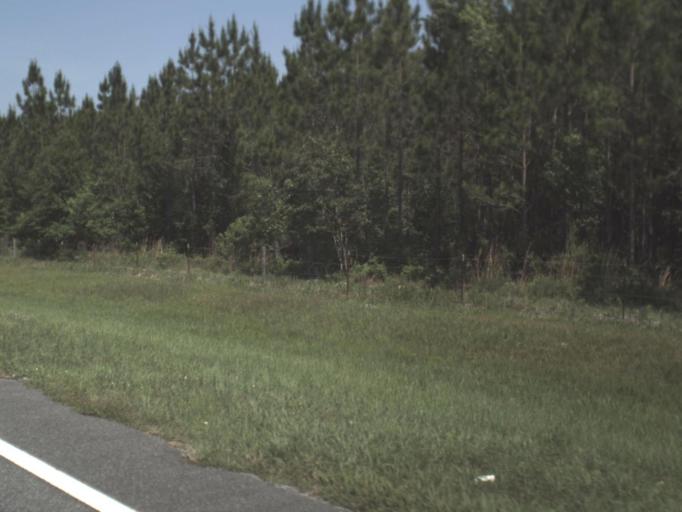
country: US
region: Florida
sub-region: Clay County
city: Asbury Lake
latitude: 29.9780
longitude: -81.8779
